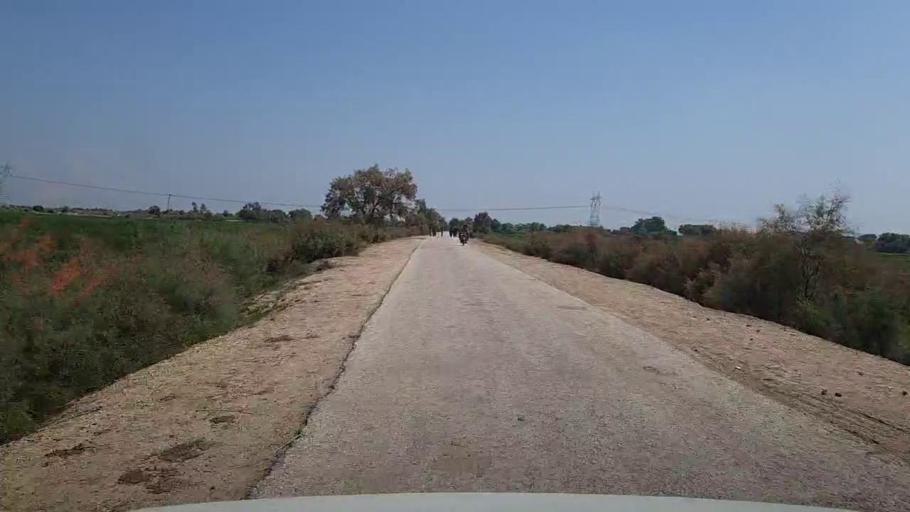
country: PK
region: Sindh
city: Kandhkot
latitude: 28.3083
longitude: 69.3418
